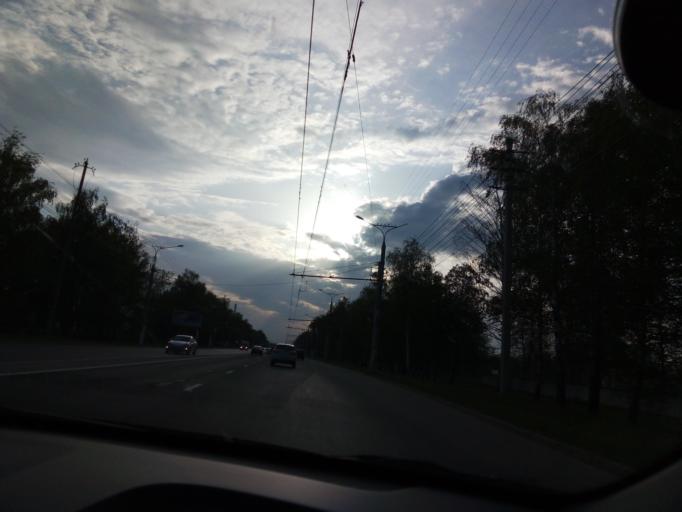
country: RU
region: Chuvashia
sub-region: Cheboksarskiy Rayon
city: Cheboksary
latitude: 56.1263
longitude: 47.3510
